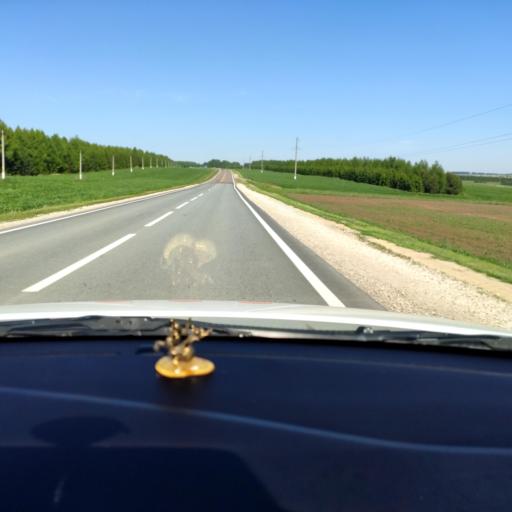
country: RU
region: Tatarstan
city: Vysokaya Gora
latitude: 56.0279
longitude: 49.2514
